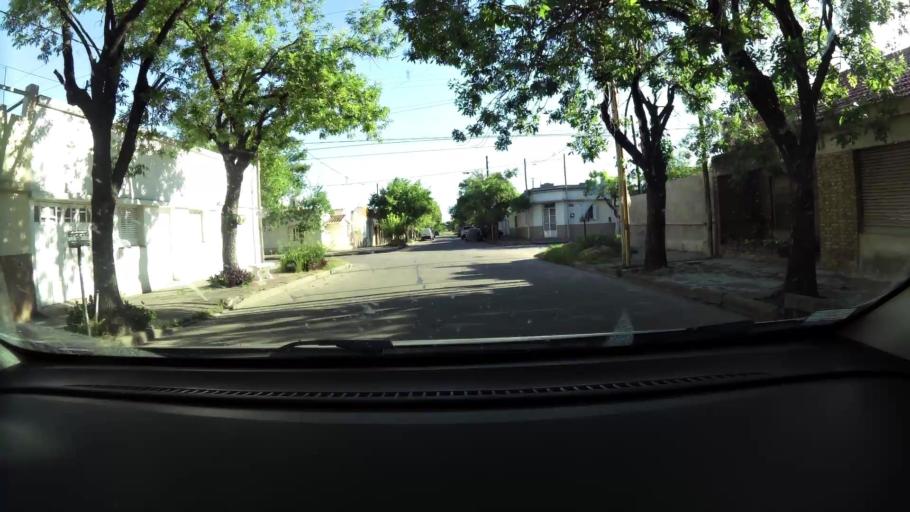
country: AR
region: Cordoba
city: San Francisco
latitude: -31.4365
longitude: -62.0910
